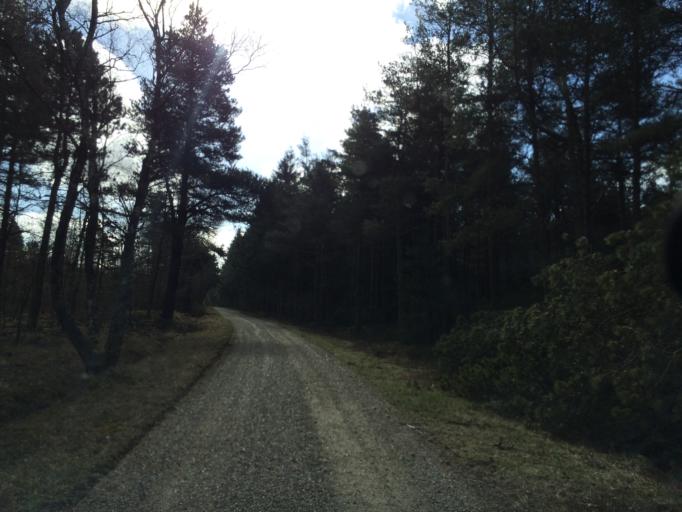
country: DK
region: Central Jutland
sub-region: Holstebro Kommune
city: Ulfborg
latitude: 56.2768
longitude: 8.4206
